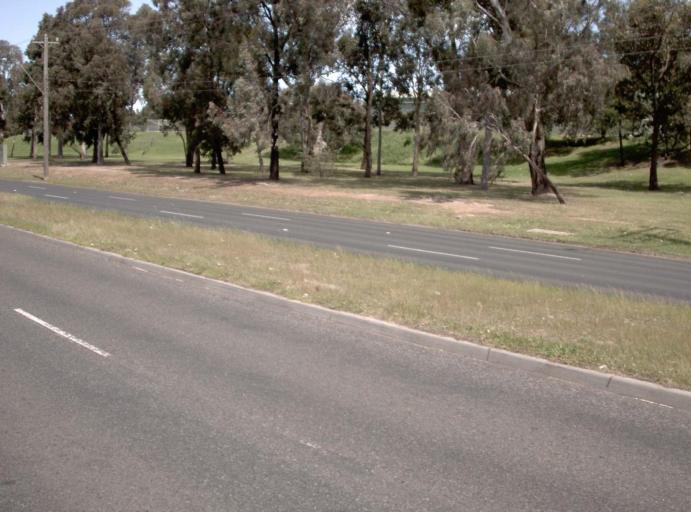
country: AU
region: Victoria
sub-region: Monash
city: Notting Hill
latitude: -37.9129
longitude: 145.1409
